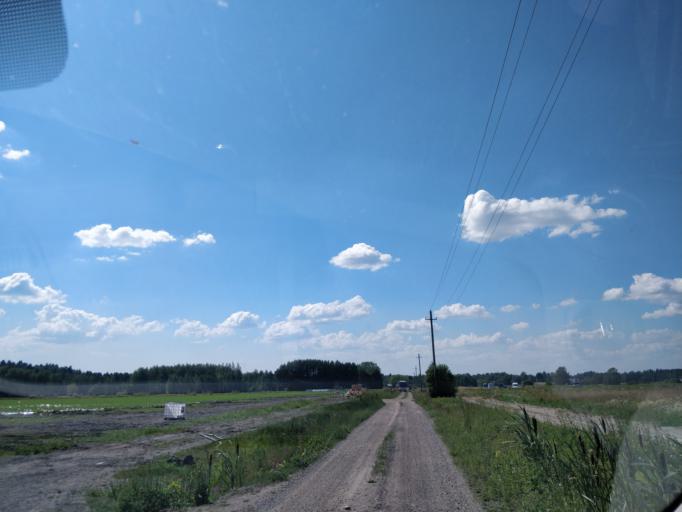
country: FI
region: Uusimaa
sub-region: Helsinki
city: Vantaa
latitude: 60.3070
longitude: 25.0785
